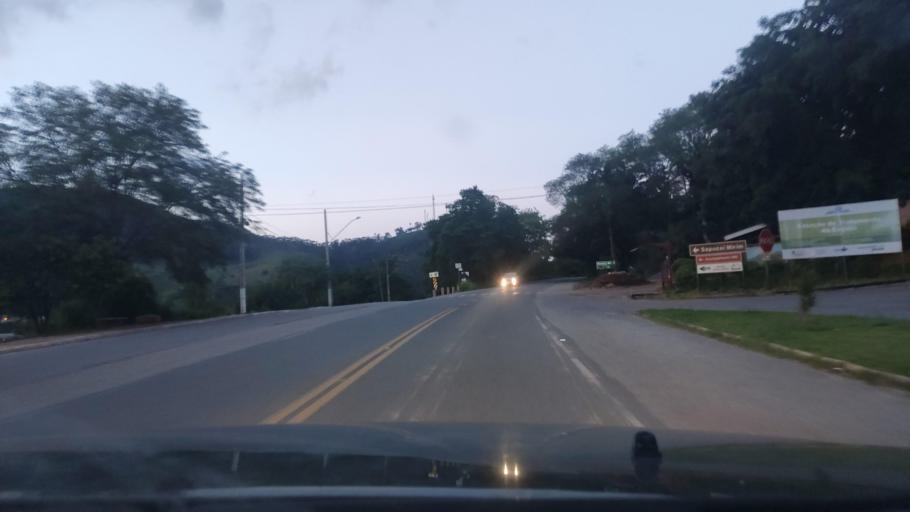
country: BR
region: Sao Paulo
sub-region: Campos Do Jordao
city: Campos do Jordao
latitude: -22.7539
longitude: -45.7436
